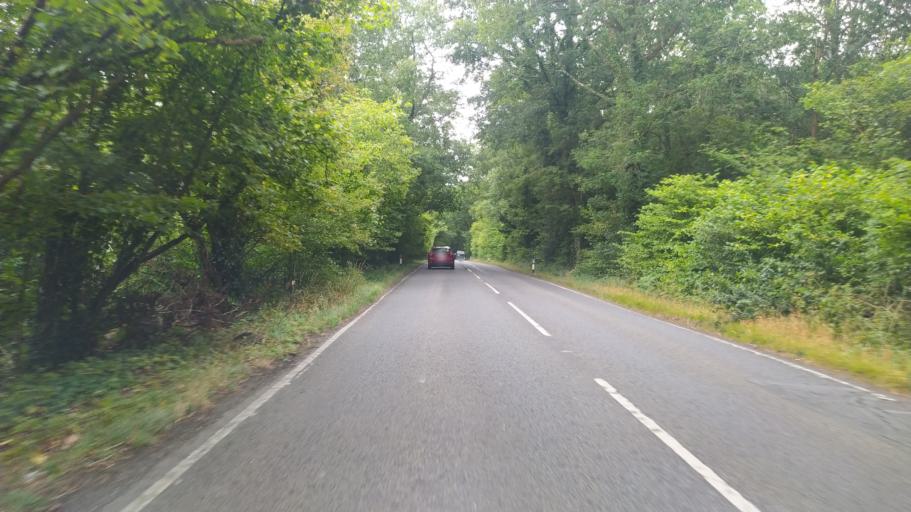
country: GB
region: England
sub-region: Hampshire
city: Havant
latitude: 50.8947
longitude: -0.9797
